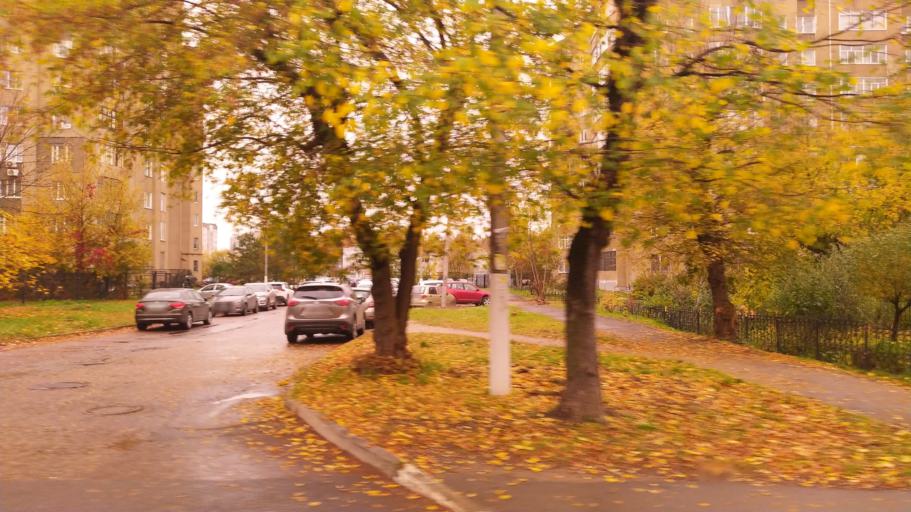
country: RU
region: Tverskaya
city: Tver
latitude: 56.8451
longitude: 35.9033
